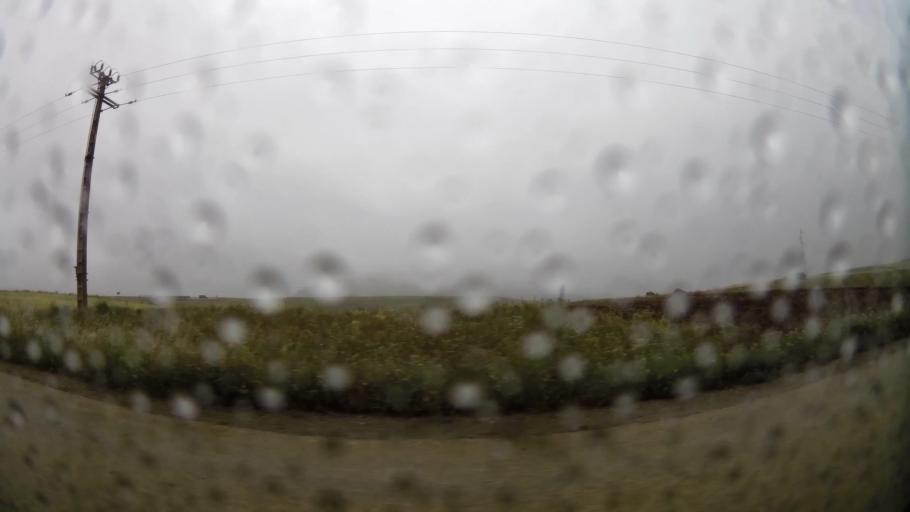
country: MA
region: Oriental
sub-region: Nador
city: Boudinar
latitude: 35.1293
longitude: -3.6471
